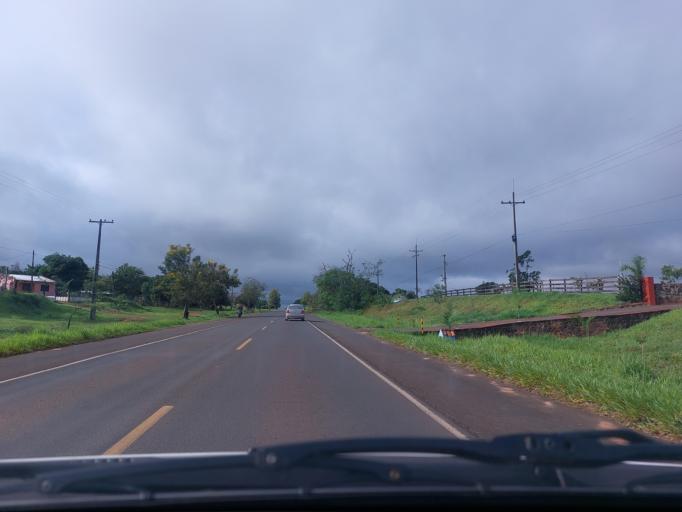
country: PY
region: San Pedro
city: Guayaybi
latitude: -24.5956
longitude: -56.3916
